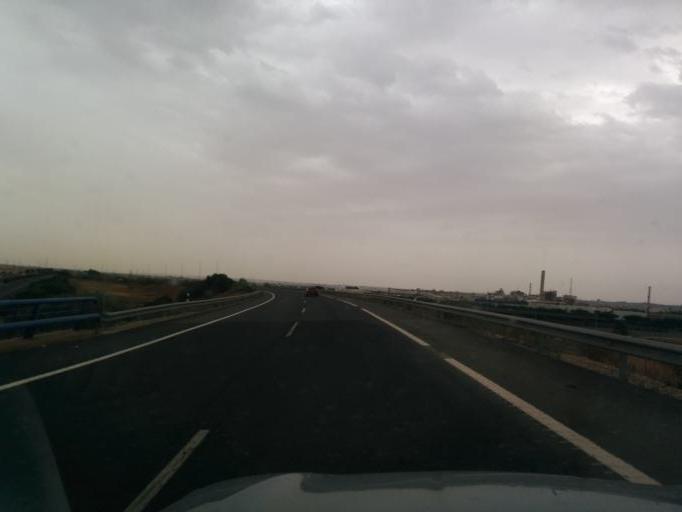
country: ES
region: Andalusia
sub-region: Provincia de Huelva
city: San Juan del Puerto
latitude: 37.3118
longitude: -6.8789
